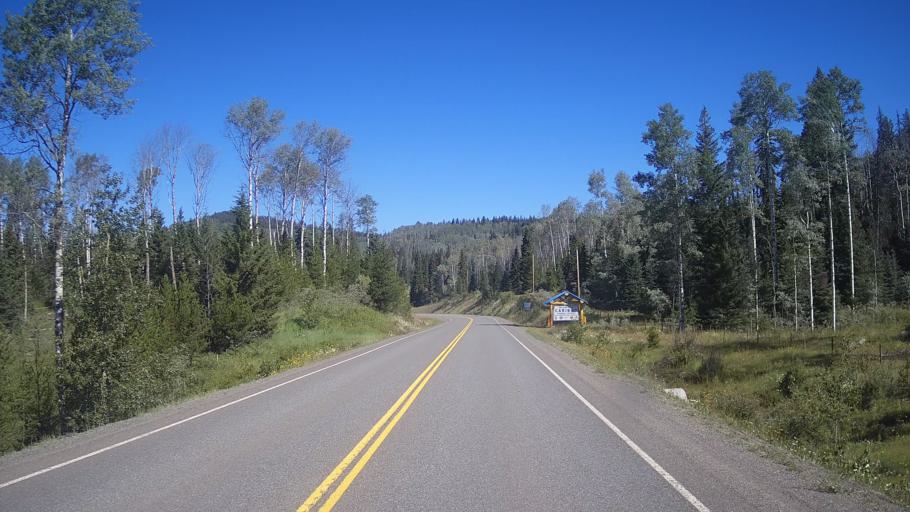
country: CA
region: British Columbia
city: Kamloops
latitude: 51.4874
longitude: -120.5644
